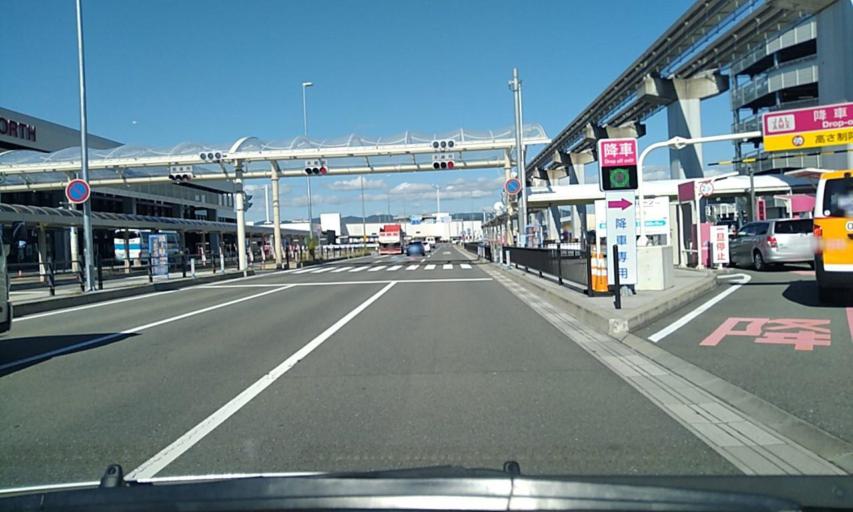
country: JP
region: Osaka
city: Toyonaka
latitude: 34.7918
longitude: 135.4413
